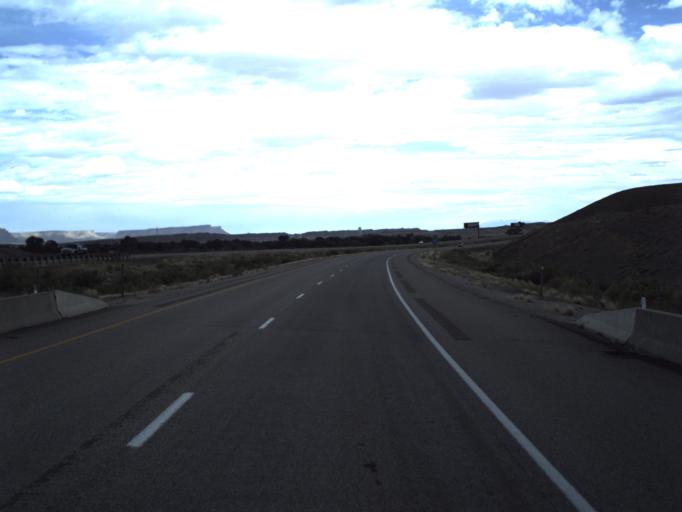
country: US
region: Utah
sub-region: Carbon County
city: East Carbon City
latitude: 38.9904
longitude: -110.1745
